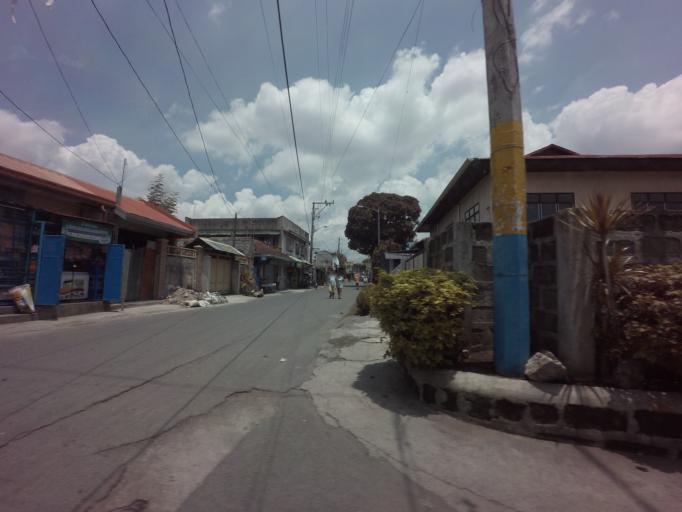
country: PH
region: Calabarzon
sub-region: Province of Laguna
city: San Pedro
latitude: 14.3884
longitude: 121.0500
